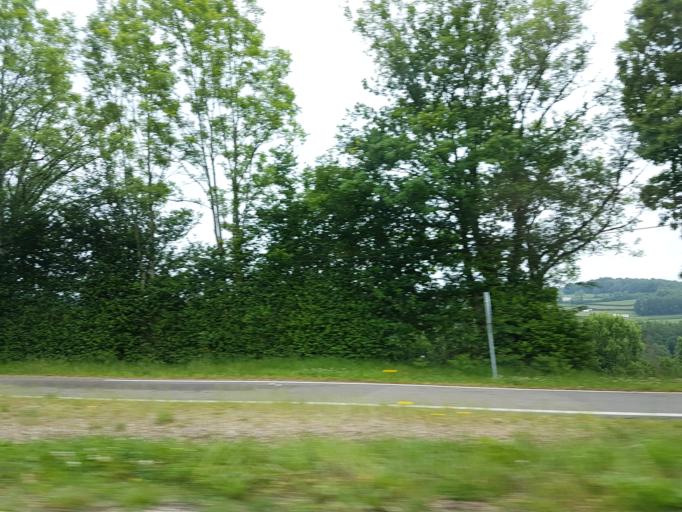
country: FR
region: Bourgogne
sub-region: Departement de la Nievre
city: Chateau-Chinon(Ville)
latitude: 47.0501
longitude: 3.9824
